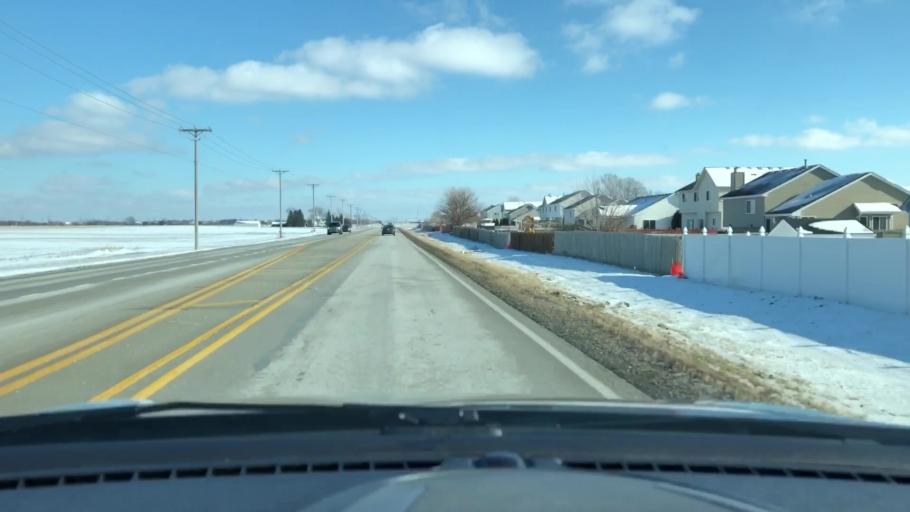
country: US
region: Illinois
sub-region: Will County
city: New Lenox
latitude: 41.4828
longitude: -87.9794
